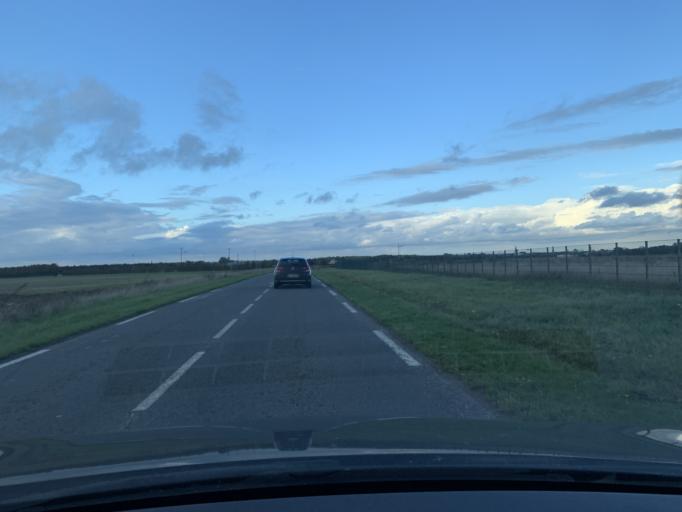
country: FR
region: Nord-Pas-de-Calais
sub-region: Departement du Nord
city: Proville
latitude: 50.1493
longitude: 3.2105
